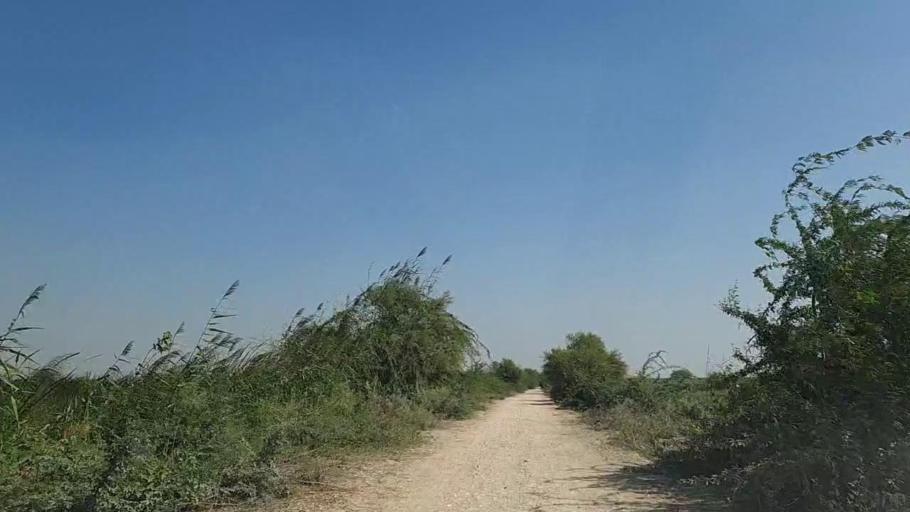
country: PK
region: Sindh
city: Daro Mehar
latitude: 24.7268
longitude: 68.1888
